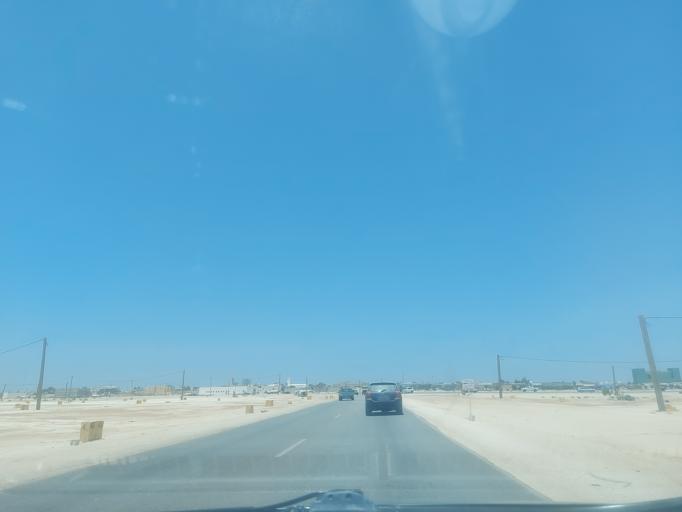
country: MR
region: Nouakchott
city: Nouakchott
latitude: 18.0870
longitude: -15.9548
